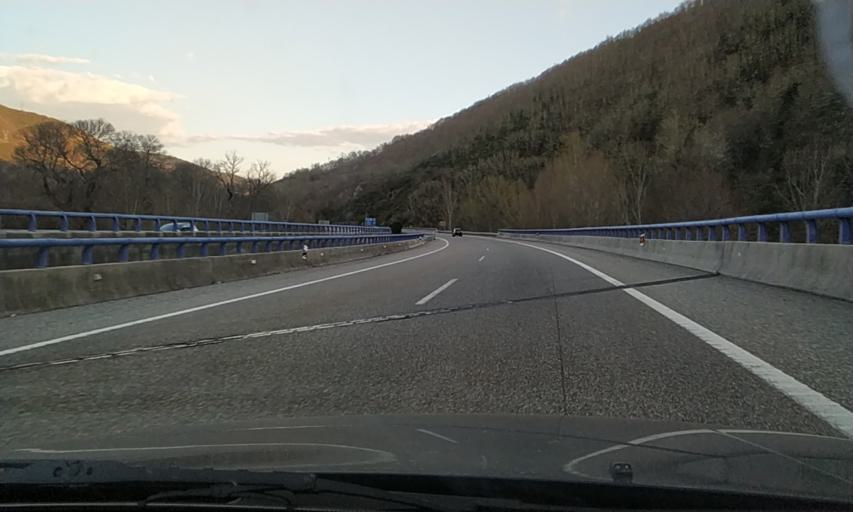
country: ES
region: Castille and Leon
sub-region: Provincia de Leon
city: Trabadelo
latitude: 42.6492
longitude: -6.8888
